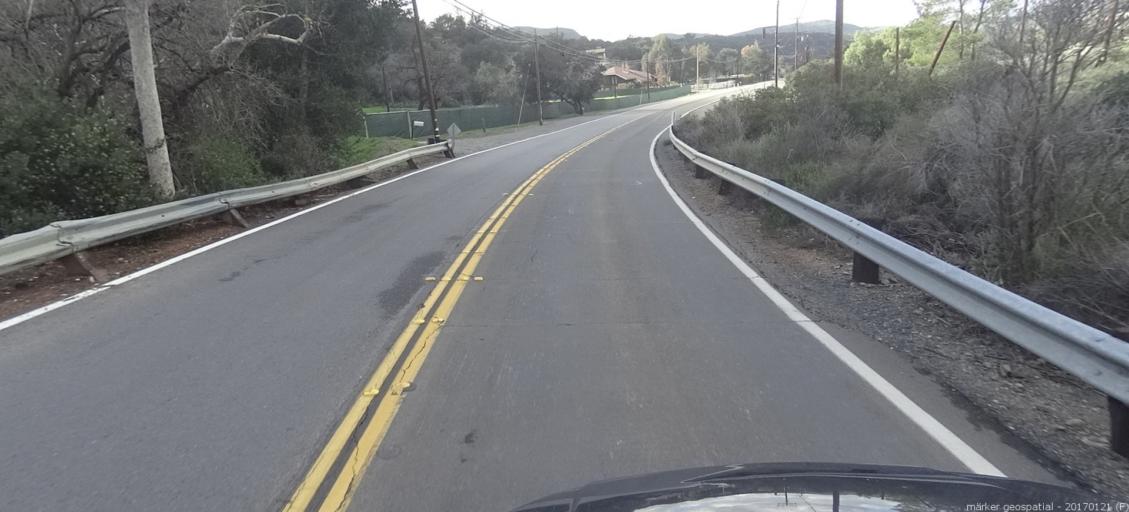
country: US
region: California
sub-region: Orange County
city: Foothill Ranch
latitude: 33.7456
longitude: -117.6506
